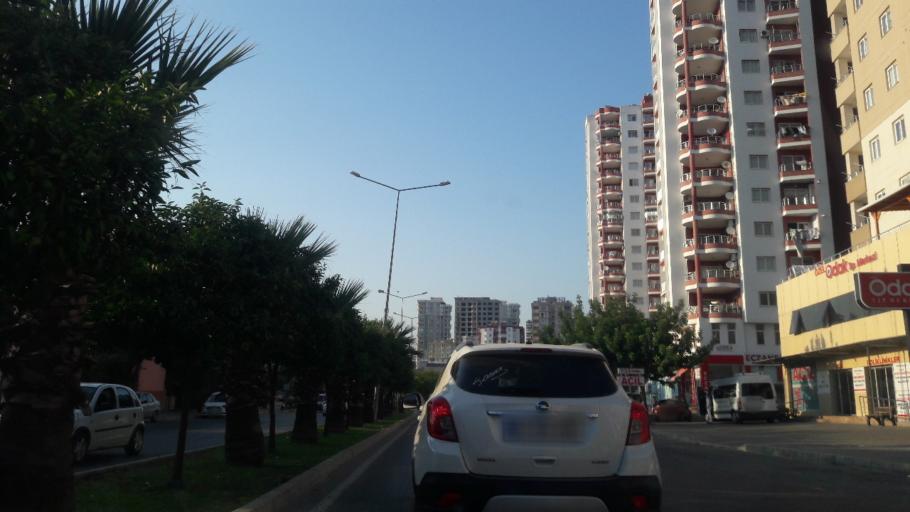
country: TR
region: Adana
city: Seyhan
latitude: 37.0126
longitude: 35.2879
